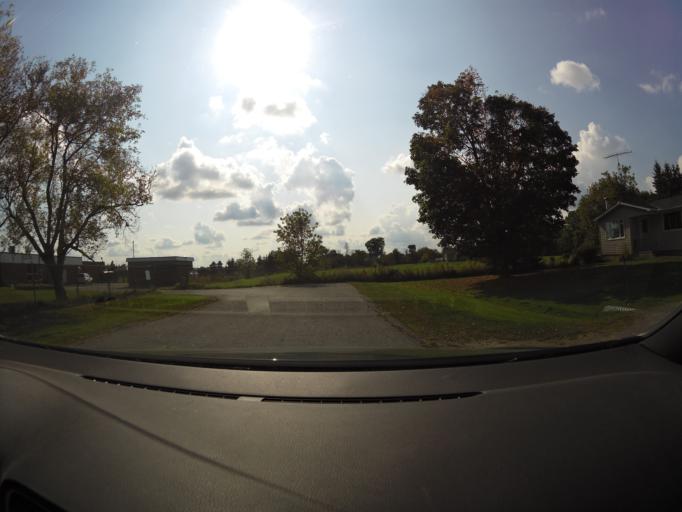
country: CA
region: Ontario
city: Arnprior
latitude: 45.3903
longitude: -76.1877
